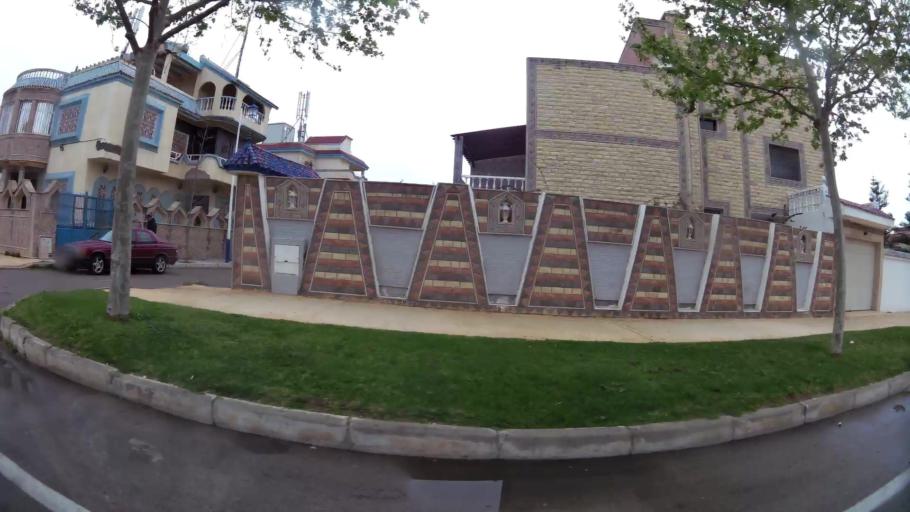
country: MA
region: Tanger-Tetouan
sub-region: Tetouan
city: Martil
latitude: 35.6355
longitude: -5.2879
